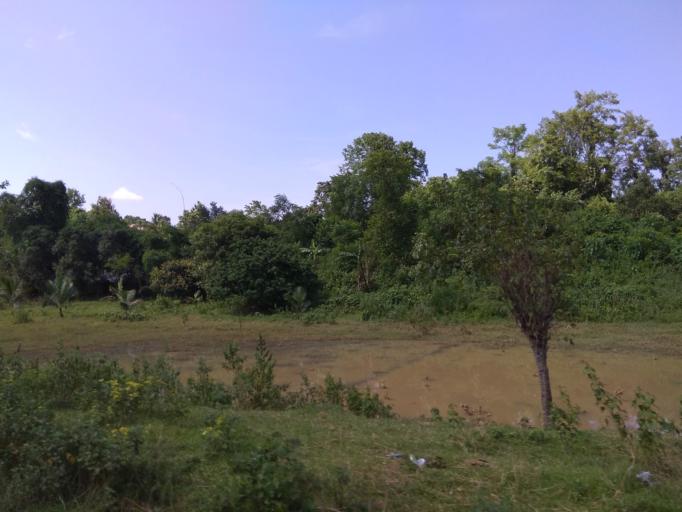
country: BD
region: Chittagong
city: Khagrachhari
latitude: 23.0350
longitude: 92.0072
